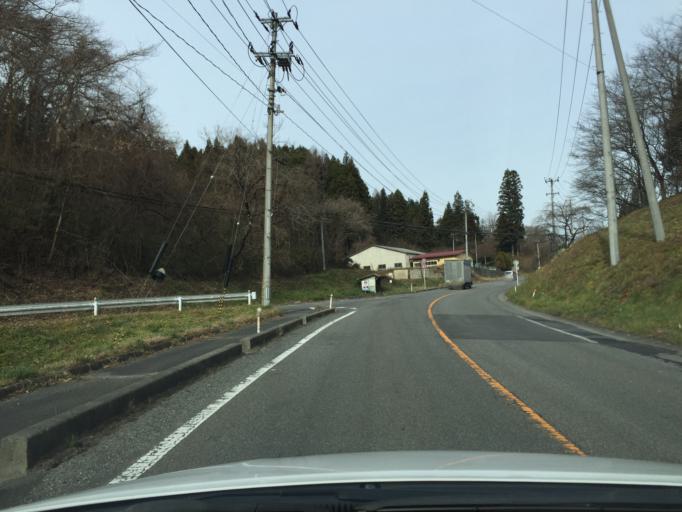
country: JP
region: Fukushima
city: Funehikimachi-funehiki
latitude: 37.2636
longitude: 140.6299
